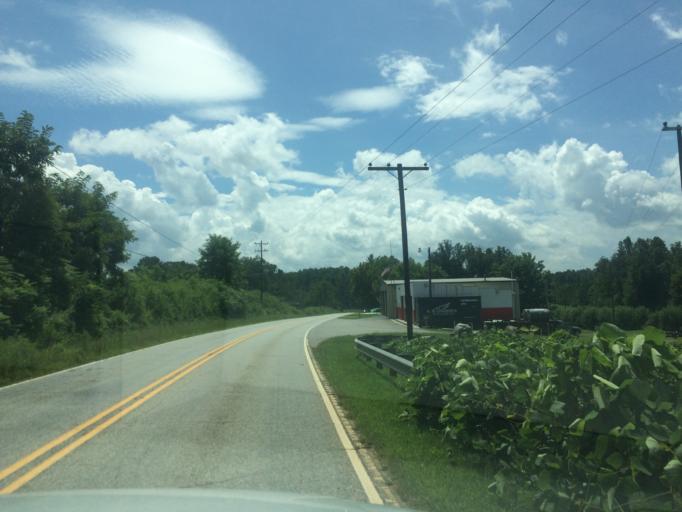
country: US
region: North Carolina
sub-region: Rutherford County
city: Lake Lure
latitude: 35.3732
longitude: -82.1858
